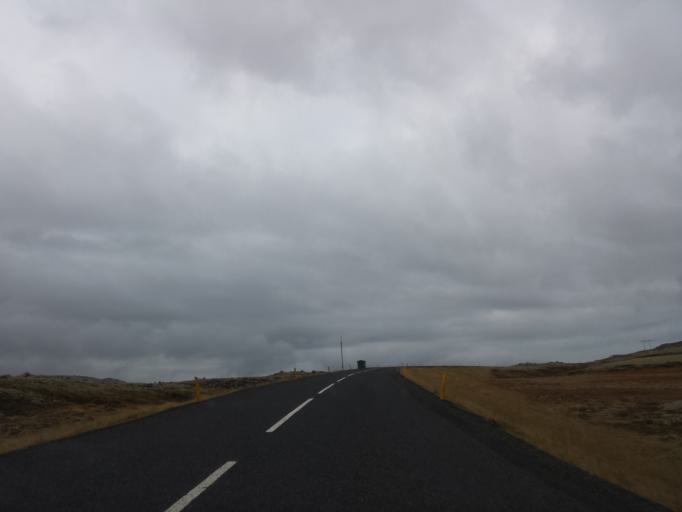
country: IS
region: West
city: Stykkisholmur
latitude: 64.9061
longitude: -22.8592
